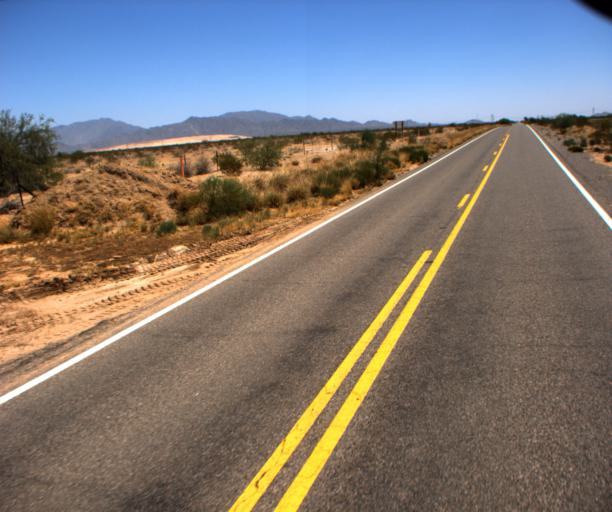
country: US
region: Arizona
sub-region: Pinal County
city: Maricopa
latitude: 33.0438
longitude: -112.3176
